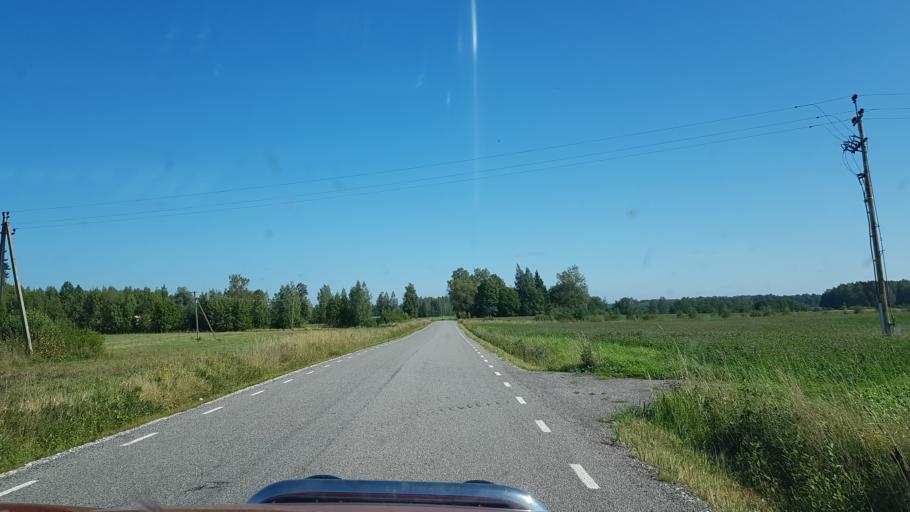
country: EE
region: Polvamaa
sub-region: Polva linn
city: Polva
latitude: 58.2147
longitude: 27.1849
